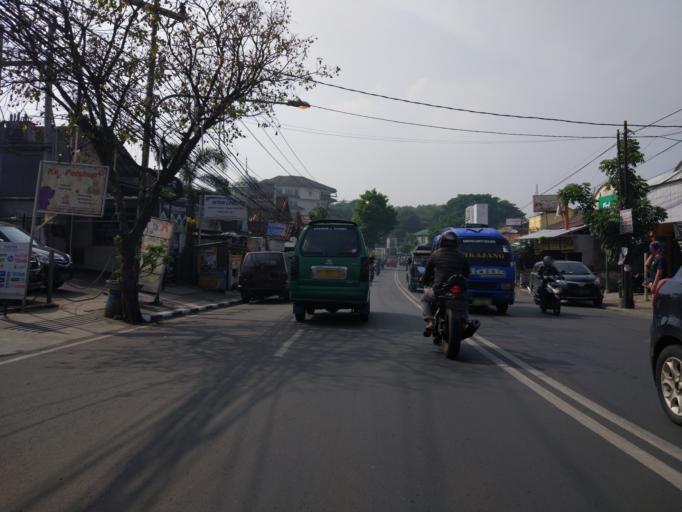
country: ID
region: West Java
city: Cileunyi
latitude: -6.9319
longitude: 107.7148
